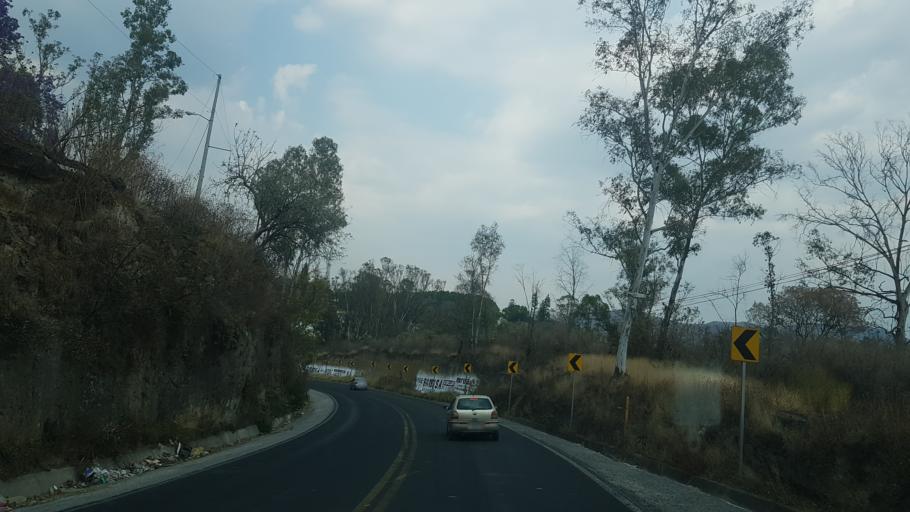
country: MX
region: Puebla
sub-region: Santa Isabel Cholula
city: Santa Ana Acozautla
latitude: 18.9463
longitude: -98.3894
